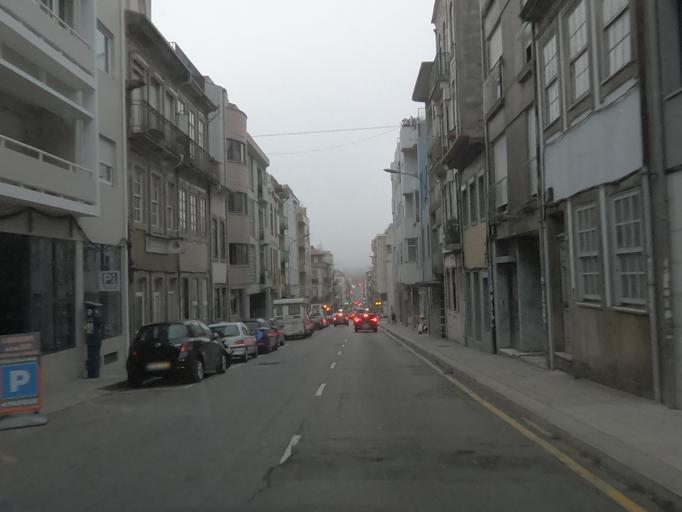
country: PT
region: Porto
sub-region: Porto
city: Porto
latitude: 41.1544
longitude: -8.6193
